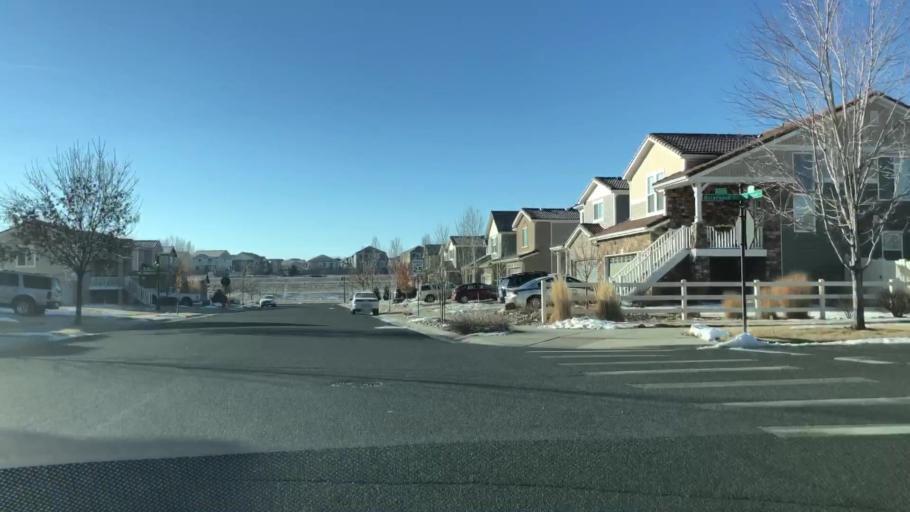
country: US
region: Colorado
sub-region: Larimer County
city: Loveland
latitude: 40.3908
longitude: -104.9860
